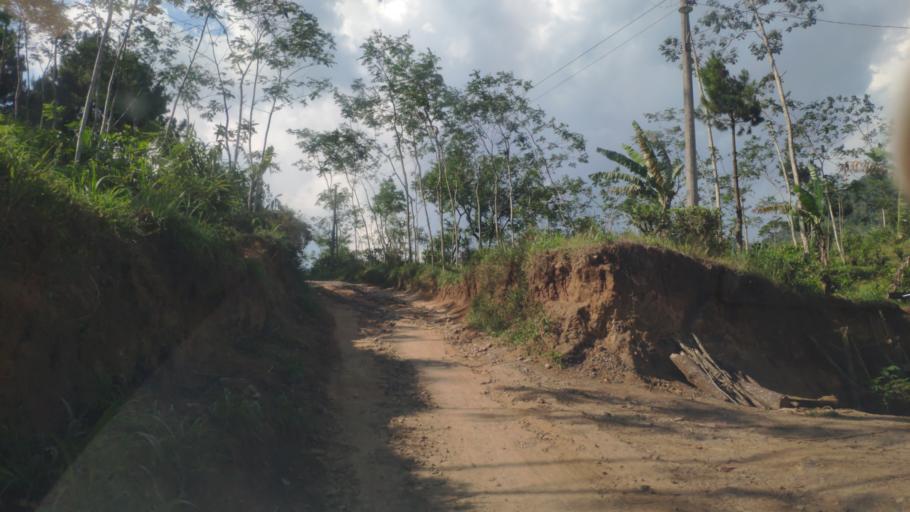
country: ID
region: Central Java
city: Buaran
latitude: -7.2228
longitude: 109.5758
